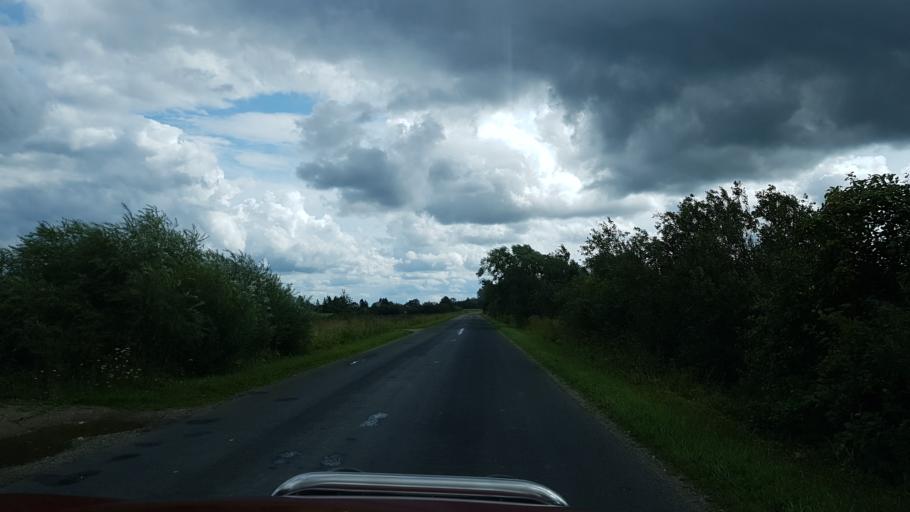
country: EE
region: Laeaene
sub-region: Lihula vald
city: Lihula
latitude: 58.7173
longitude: 23.9887
